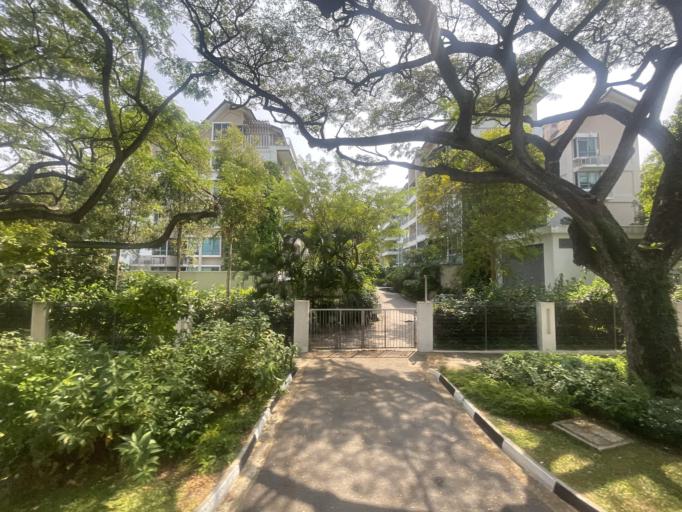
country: SG
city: Singapore
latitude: 1.2960
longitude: 103.7670
